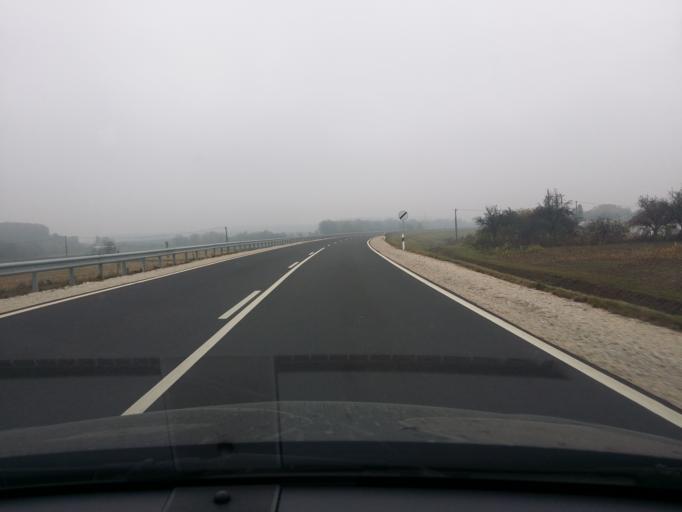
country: HU
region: Szabolcs-Szatmar-Bereg
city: Kalmanhaza
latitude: 47.9217
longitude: 21.6438
